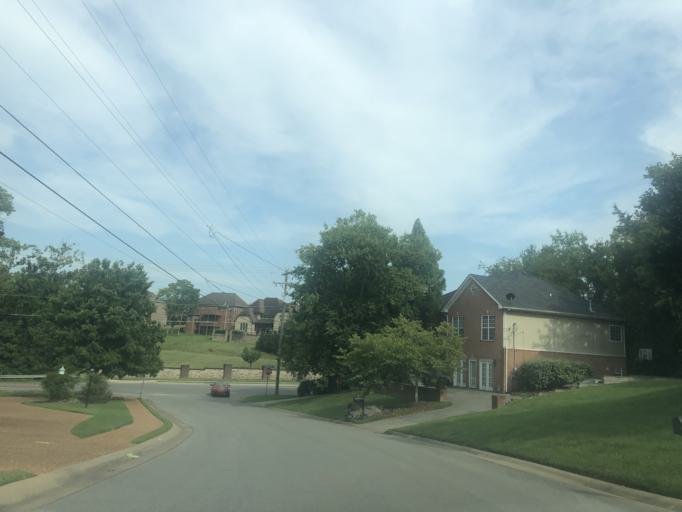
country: US
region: Tennessee
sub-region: Wilson County
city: Green Hill
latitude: 36.1792
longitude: -86.5832
